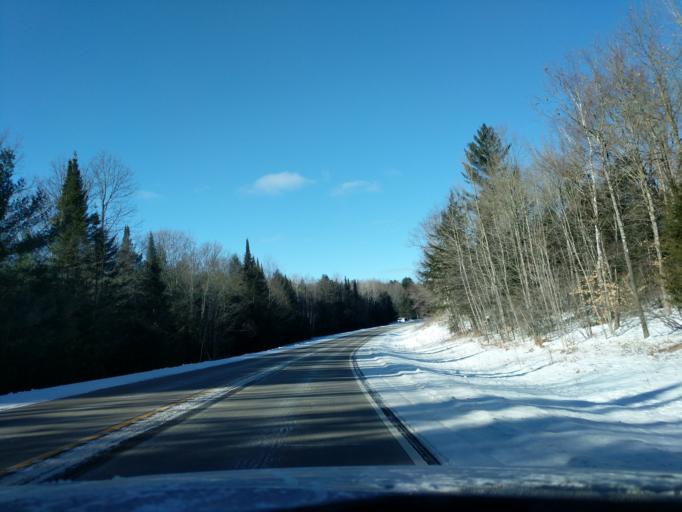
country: US
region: Wisconsin
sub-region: Menominee County
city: Keshena
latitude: 45.1299
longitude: -88.6684
